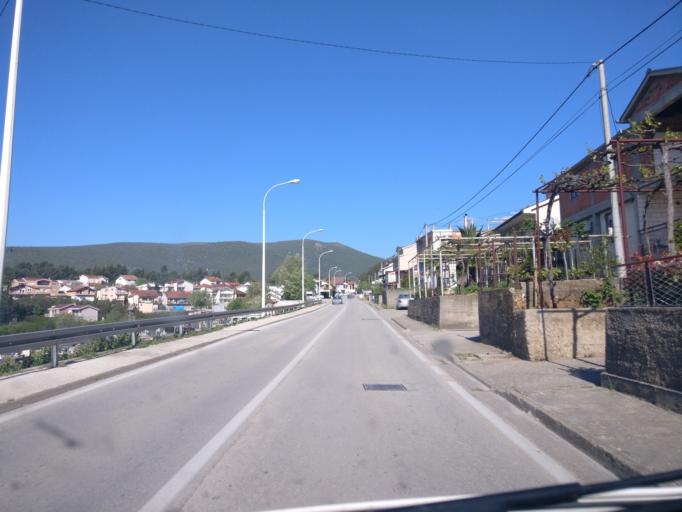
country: BA
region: Federation of Bosnia and Herzegovina
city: Capljina
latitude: 43.1187
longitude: 17.6914
